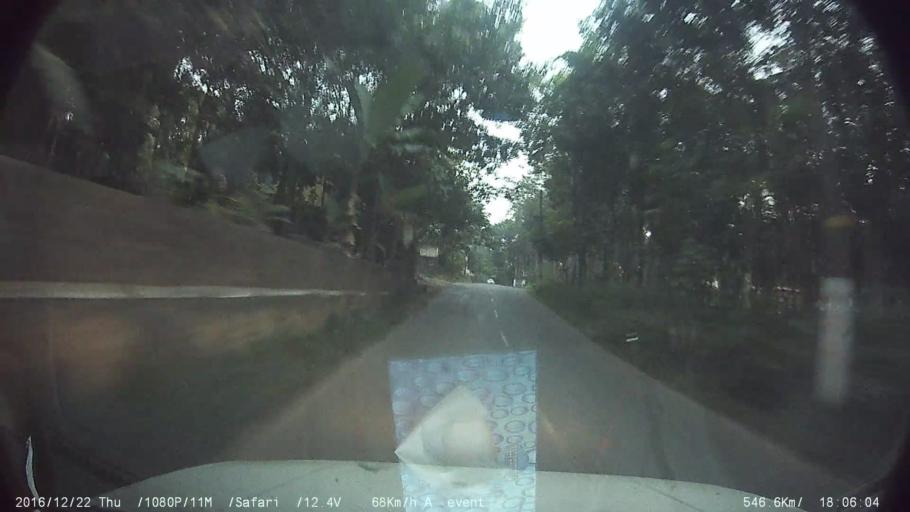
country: IN
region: Kerala
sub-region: Kottayam
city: Palackattumala
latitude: 9.8228
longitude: 76.6081
